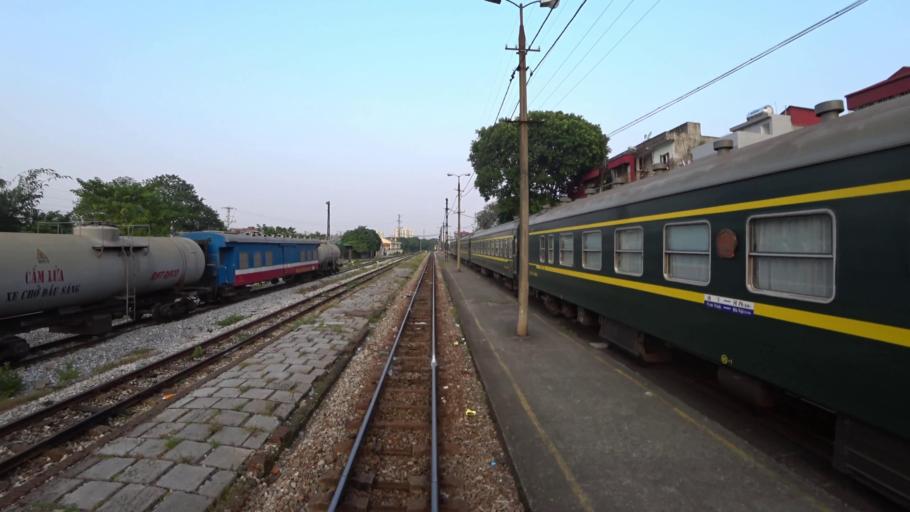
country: VN
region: Ha Noi
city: Hoan Kiem
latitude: 21.0654
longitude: 105.8967
